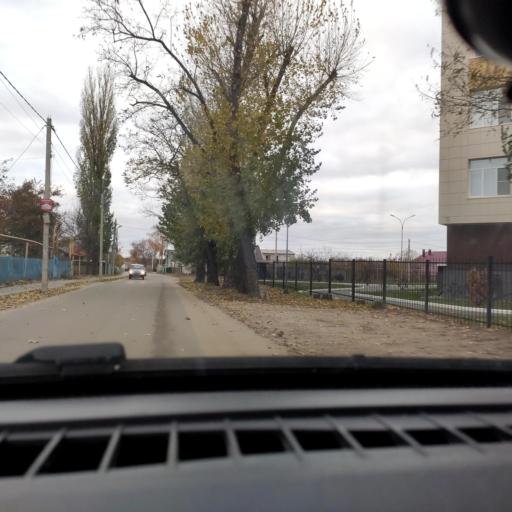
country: RU
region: Voronezj
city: Podgornoye
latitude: 51.7309
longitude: 39.1598
